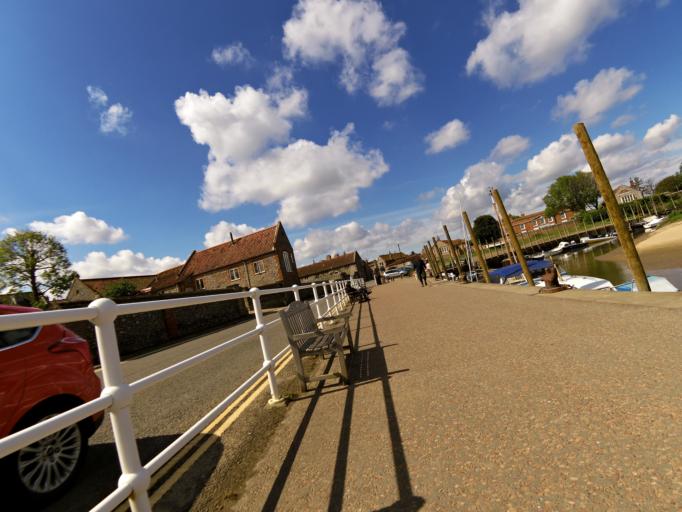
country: GB
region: England
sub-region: Norfolk
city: Briston
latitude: 52.9556
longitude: 1.0160
